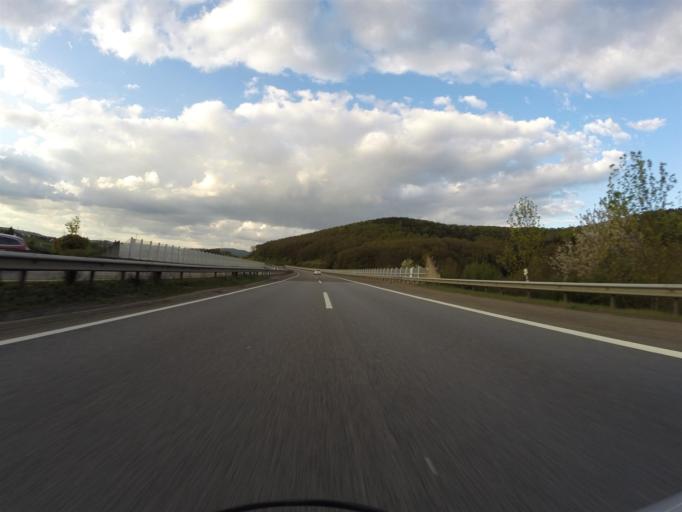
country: DE
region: Rheinland-Pfalz
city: Wartenberg-Rohrbach
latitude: 49.5388
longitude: 7.8534
